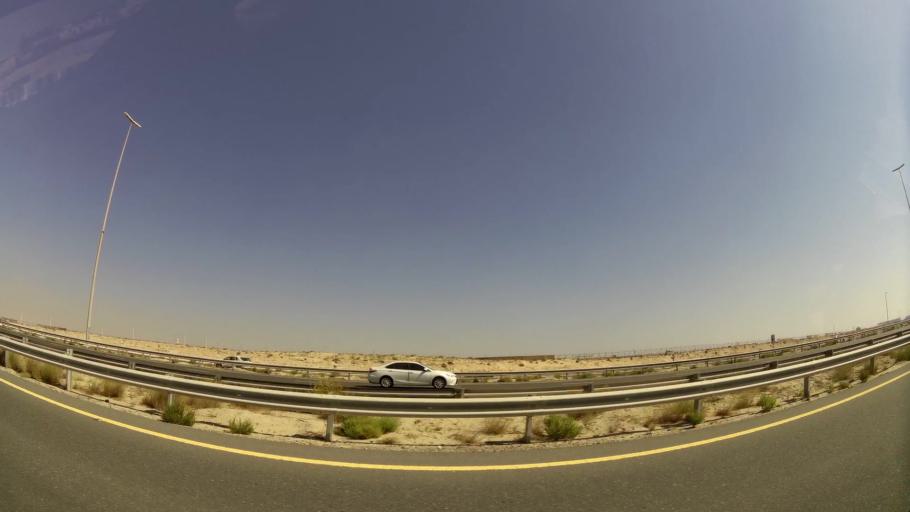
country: AE
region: Dubai
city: Dubai
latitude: 24.9443
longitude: 55.0555
